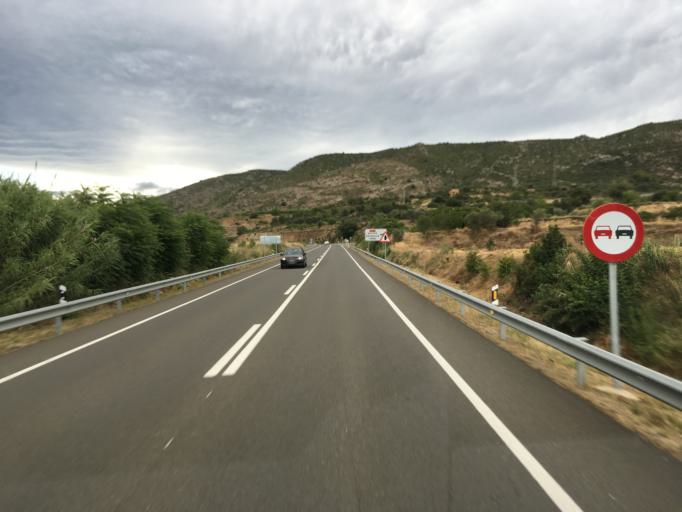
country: ES
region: Aragon
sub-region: Provincia de Huesca
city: Estada
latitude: 42.0778
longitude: 0.2350
